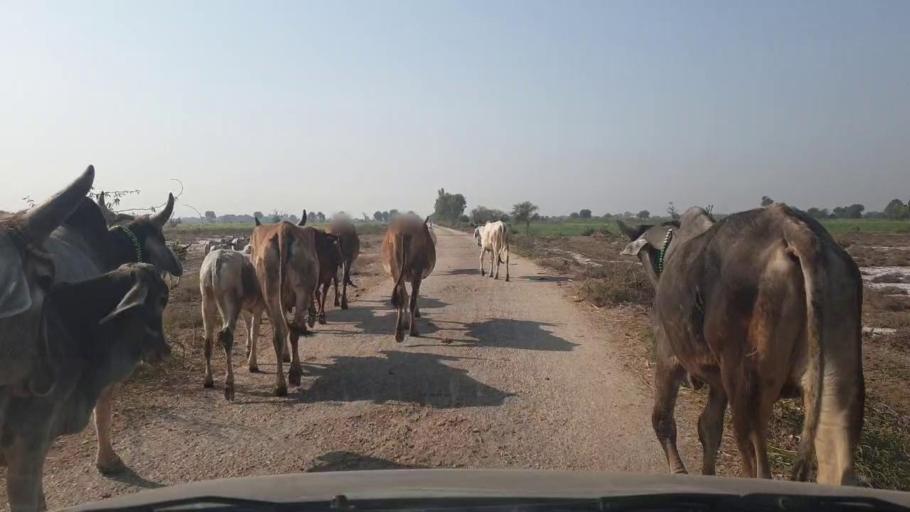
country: PK
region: Sindh
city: Mirwah Gorchani
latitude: 25.2801
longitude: 69.1227
